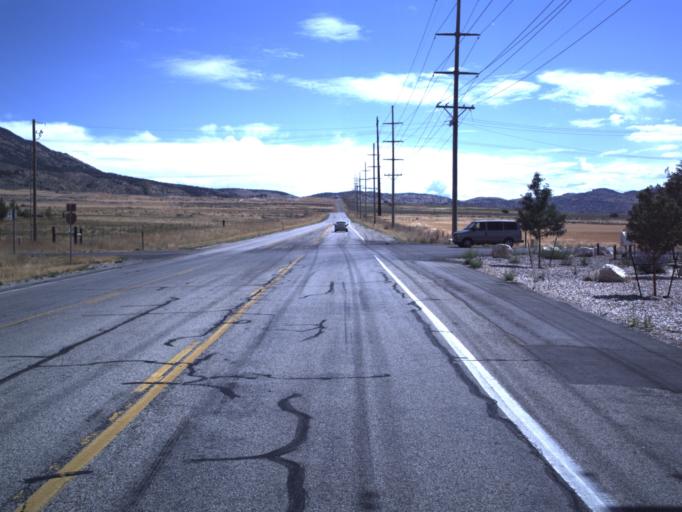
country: US
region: Utah
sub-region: Box Elder County
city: Garland
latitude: 41.8865
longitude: -112.1673
